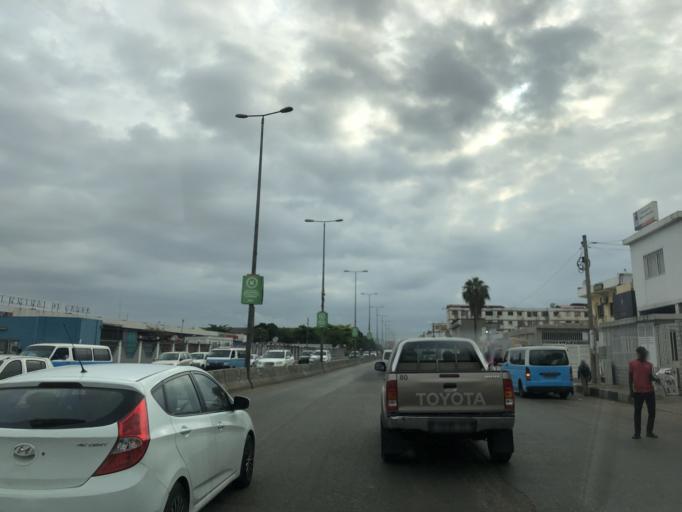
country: AO
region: Luanda
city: Luanda
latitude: -8.8461
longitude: 13.2328
